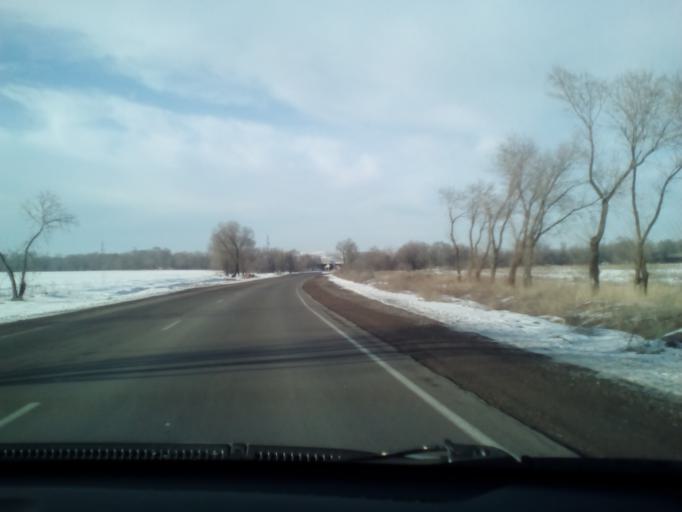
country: KZ
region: Almaty Oblysy
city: Burunday
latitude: 43.2184
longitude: 76.4114
